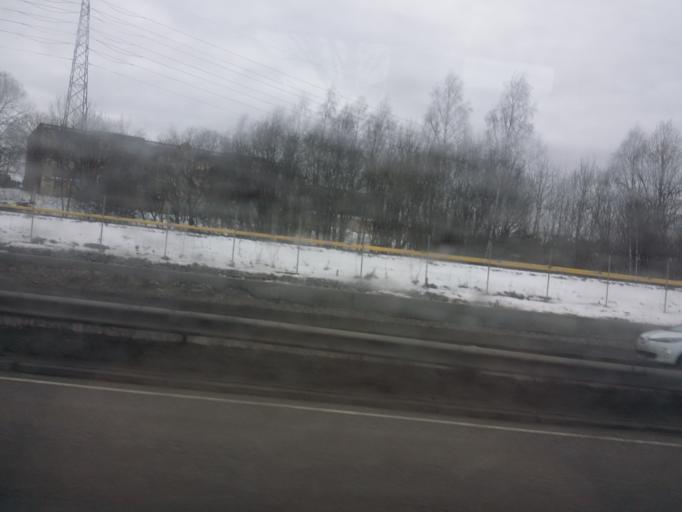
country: NO
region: Oslo
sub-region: Oslo
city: Oslo
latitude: 59.9026
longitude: 10.8197
